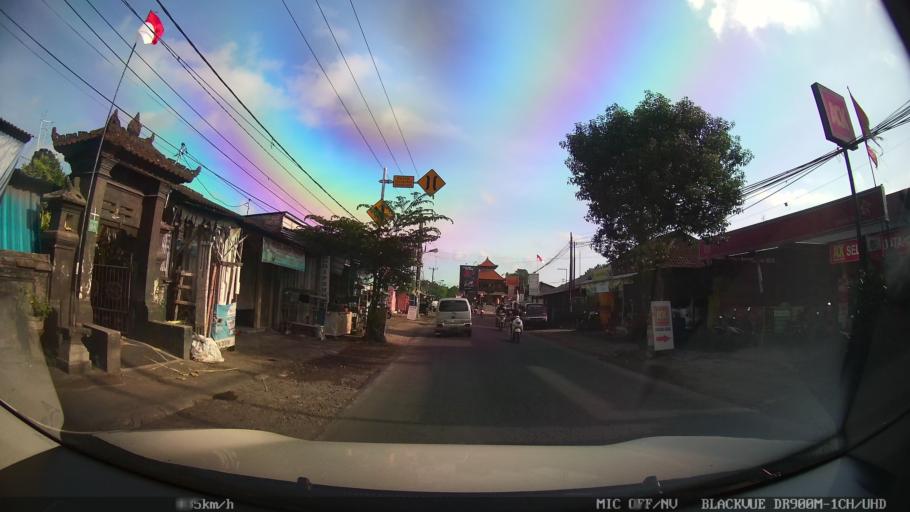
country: ID
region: Bali
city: Banjar Parekan
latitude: -8.5807
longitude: 115.2169
